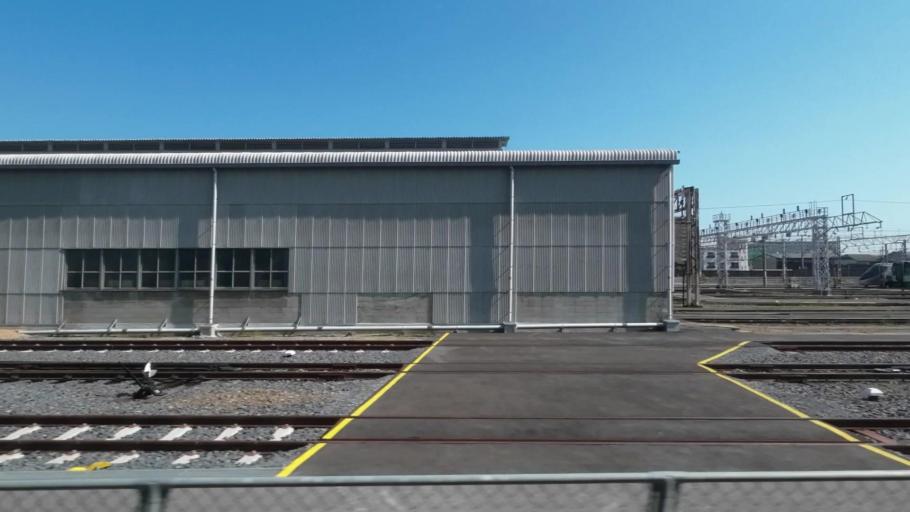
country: JP
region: Kagawa
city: Takamatsu-shi
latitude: 34.3450
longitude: 134.0239
